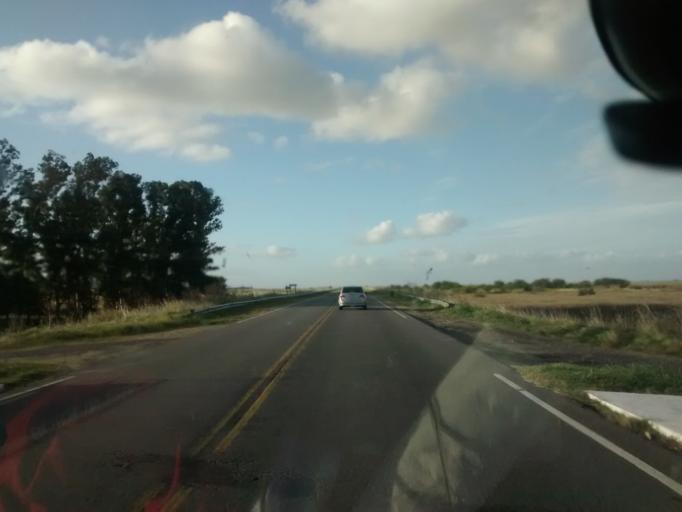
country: AR
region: Buenos Aires
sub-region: Partido de General Belgrano
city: General Belgrano
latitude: -36.1355
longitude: -58.5938
